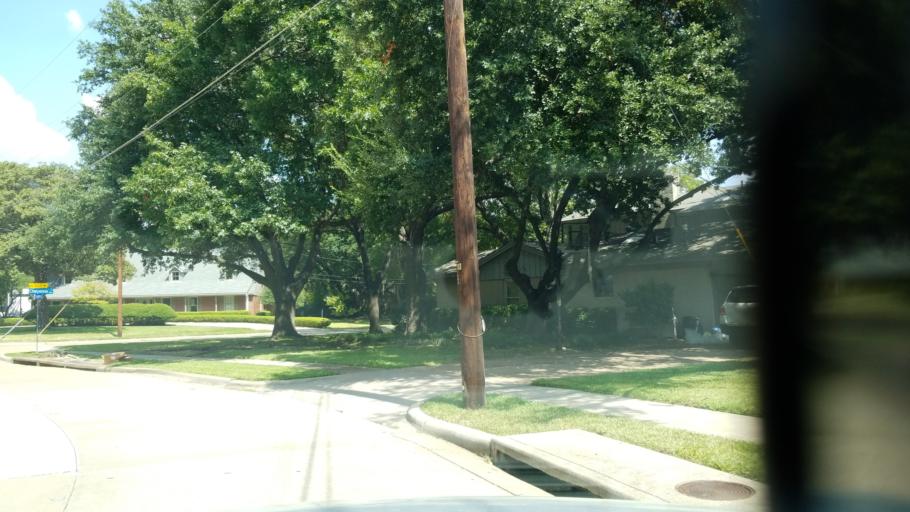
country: US
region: Texas
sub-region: Dallas County
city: Richardson
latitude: 32.9639
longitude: -96.7580
